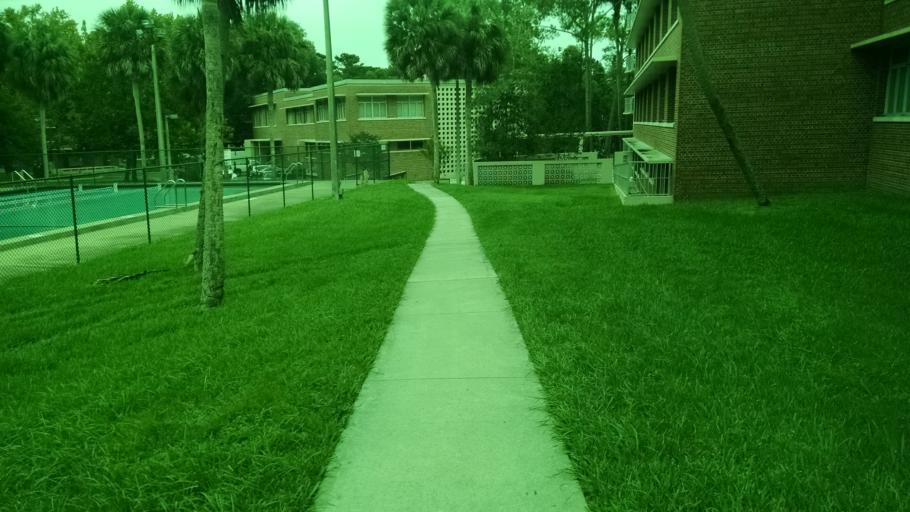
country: US
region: Florida
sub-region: Alachua County
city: Gainesville
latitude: 29.6460
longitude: -82.3520
